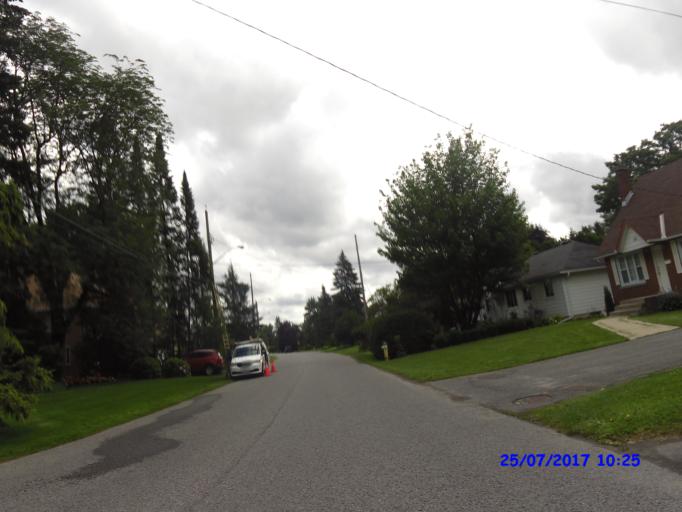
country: CA
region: Ontario
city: Ottawa
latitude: 45.3571
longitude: -75.7044
